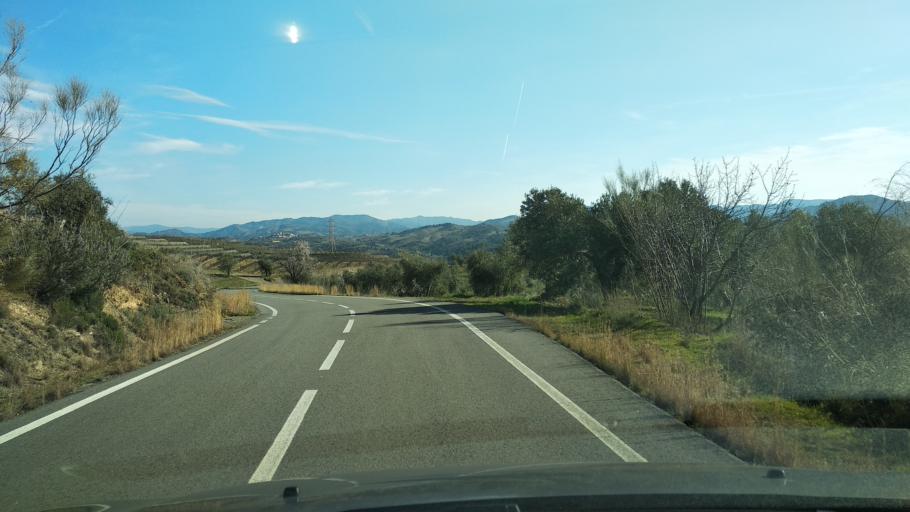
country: ES
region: Catalonia
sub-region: Provincia de Tarragona
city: el Masroig
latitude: 41.1786
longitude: 0.7343
